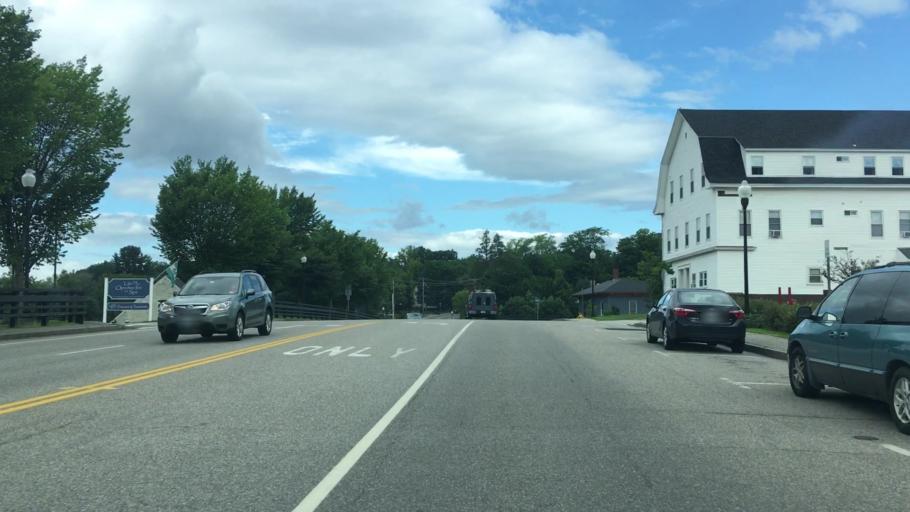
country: US
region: New Hampshire
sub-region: Belknap County
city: Laconia
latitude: 43.5480
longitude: -71.4635
